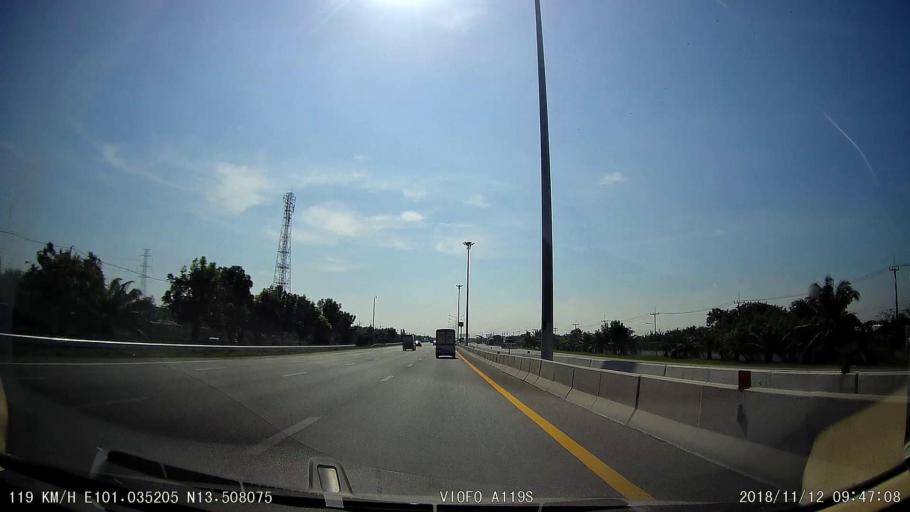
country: TH
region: Chachoengsao
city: Bang Pakong
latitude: 13.5064
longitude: 101.0367
